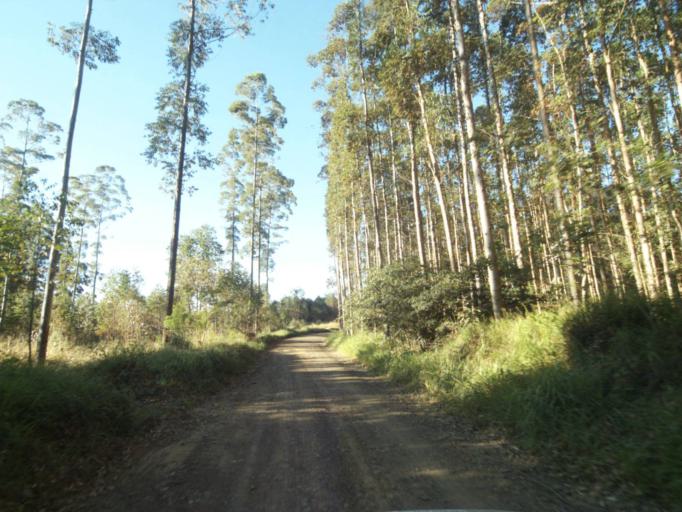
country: BR
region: Parana
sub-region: Telemaco Borba
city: Telemaco Borba
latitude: -24.4923
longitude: -50.5967
